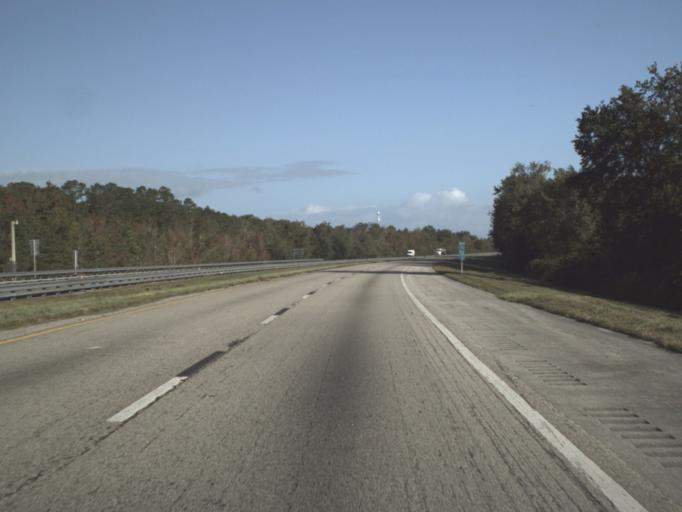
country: US
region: Florida
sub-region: Indian River County
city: Fellsmere
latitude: 27.6859
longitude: -80.8942
